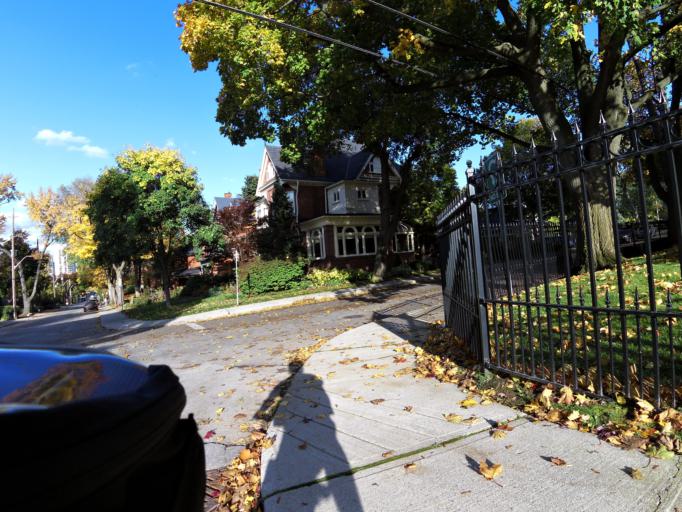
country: CA
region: Ontario
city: Hamilton
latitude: 43.2476
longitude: -79.8782
